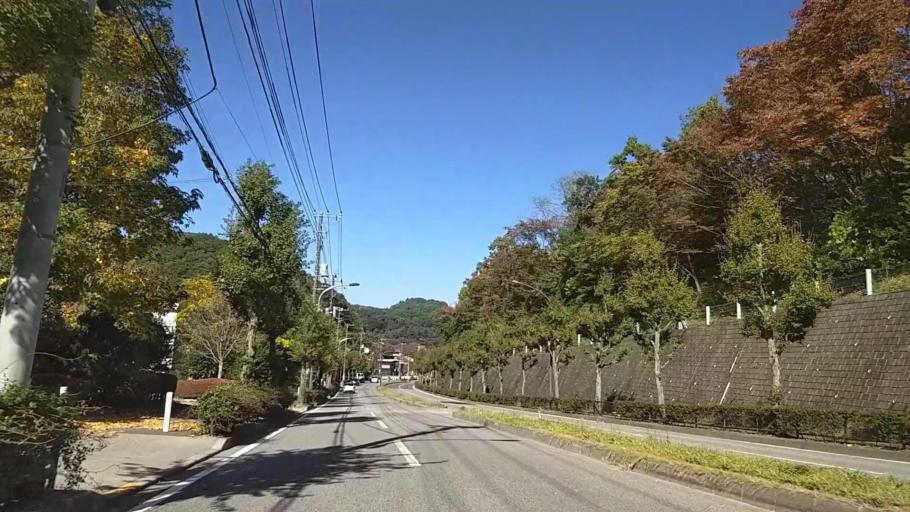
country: JP
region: Tokyo
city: Hachioji
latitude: 35.6242
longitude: 139.2863
